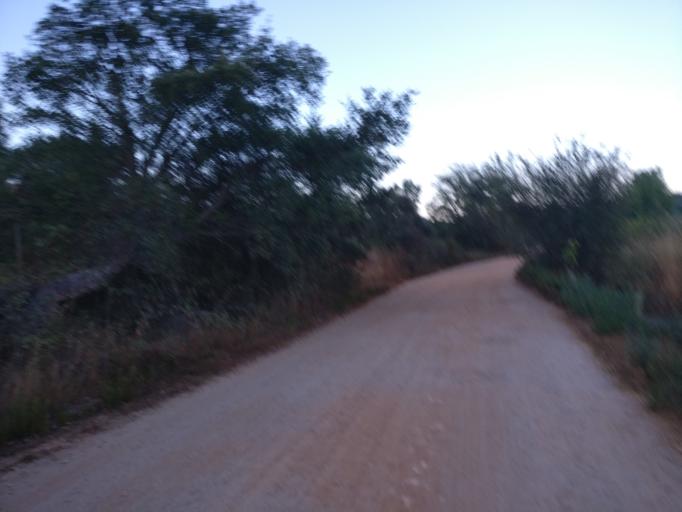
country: PT
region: Beja
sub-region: Odemira
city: Odemira
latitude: 37.7136
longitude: -8.5157
